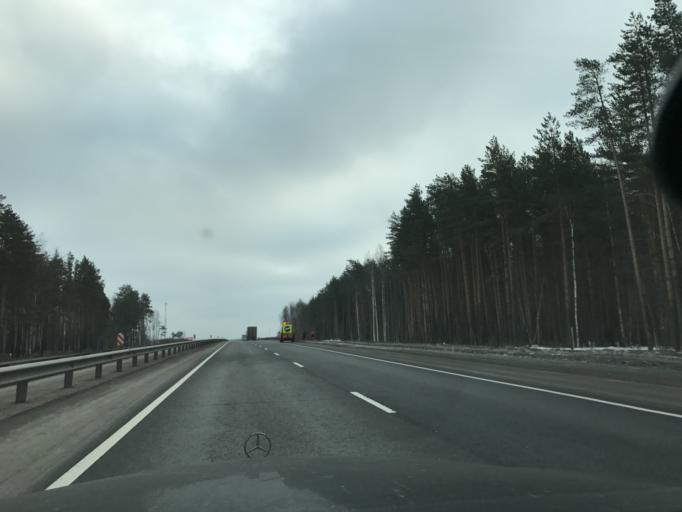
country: RU
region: Vladimir
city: Orgtrud
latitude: 56.1026
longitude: 40.7425
